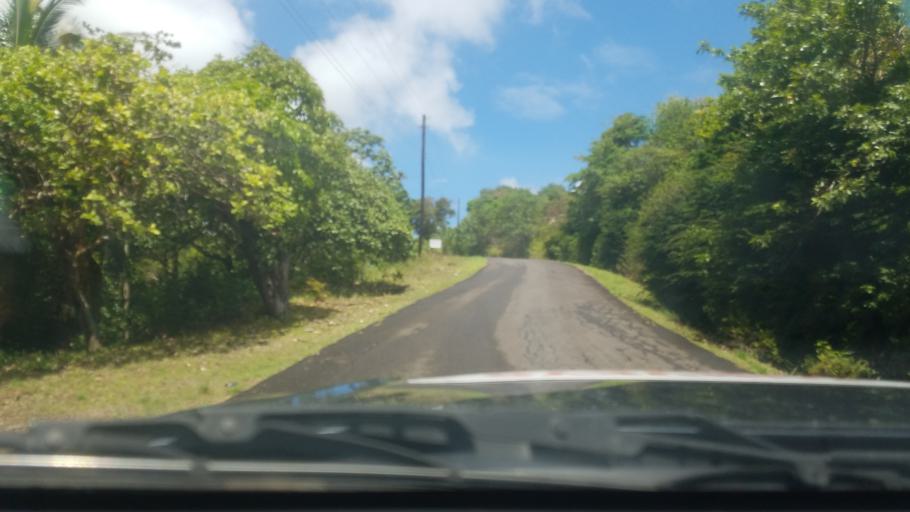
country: LC
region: Dennery Quarter
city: Dennery
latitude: 13.8989
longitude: -60.8939
